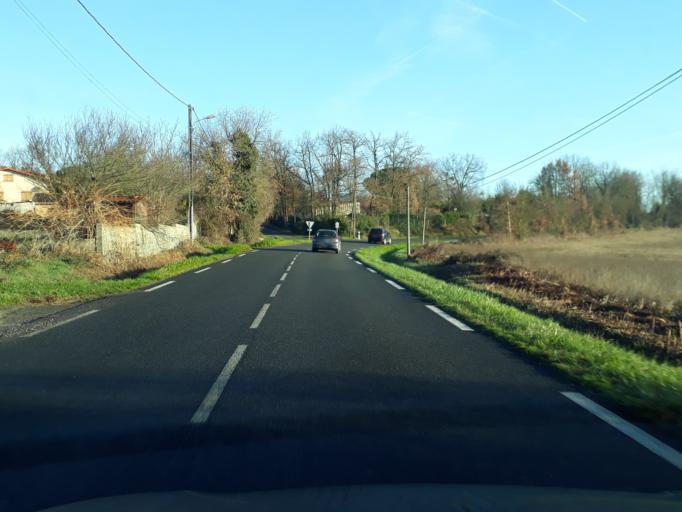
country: FR
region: Midi-Pyrenees
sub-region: Departement de la Haute-Garonne
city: Sainte-Foy-de-Peyrolieres
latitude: 43.4812
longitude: 1.1440
